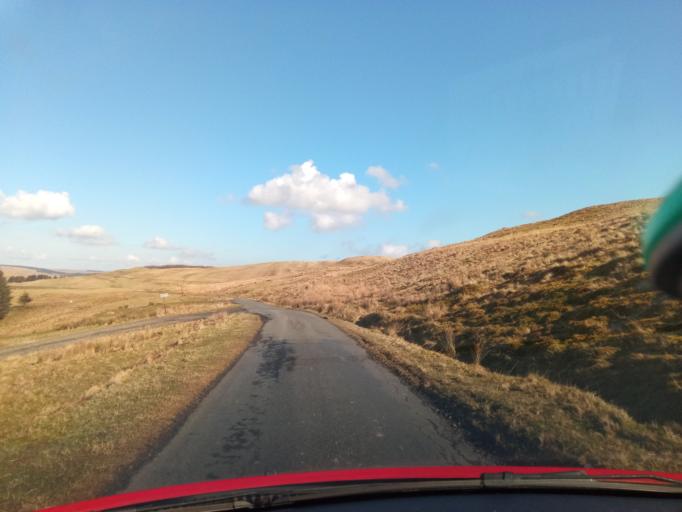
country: GB
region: Scotland
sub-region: The Scottish Borders
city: Hawick
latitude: 55.4477
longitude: -2.8873
